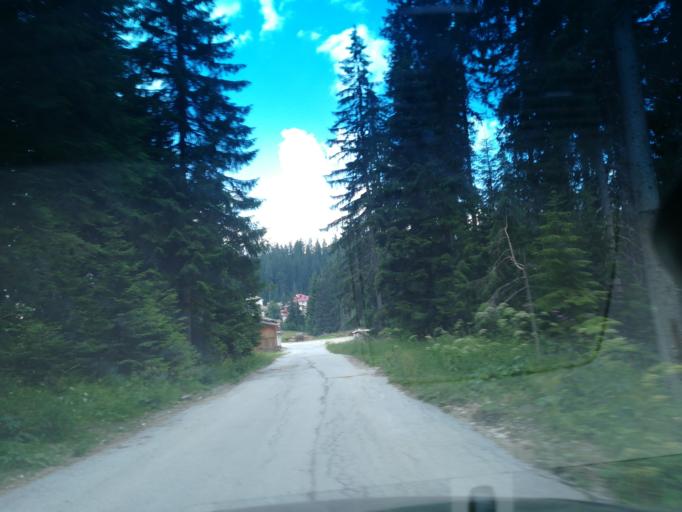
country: BG
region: Smolyan
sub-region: Obshtina Smolyan
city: Smolyan
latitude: 41.6549
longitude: 24.6832
